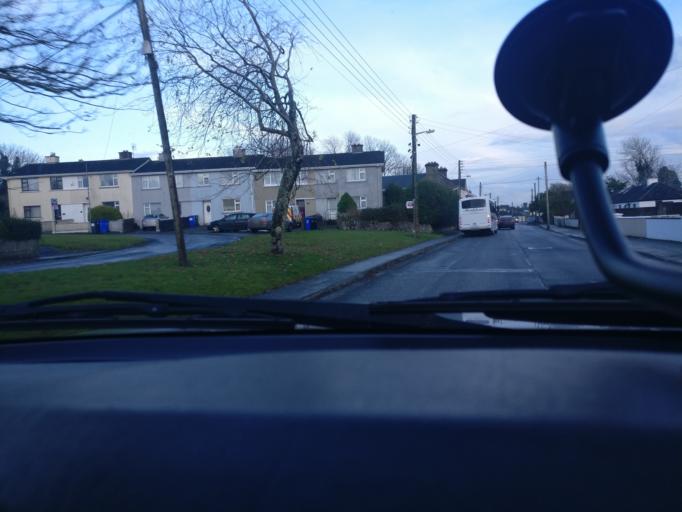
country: IE
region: Connaught
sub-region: County Galway
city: Loughrea
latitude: 53.1990
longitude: -8.5800
